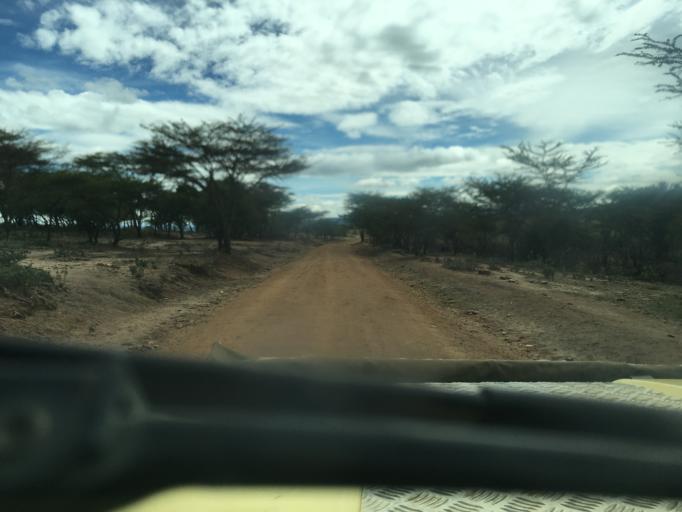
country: TZ
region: Mara
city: Mugumu
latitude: -1.8864
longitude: 35.3155
